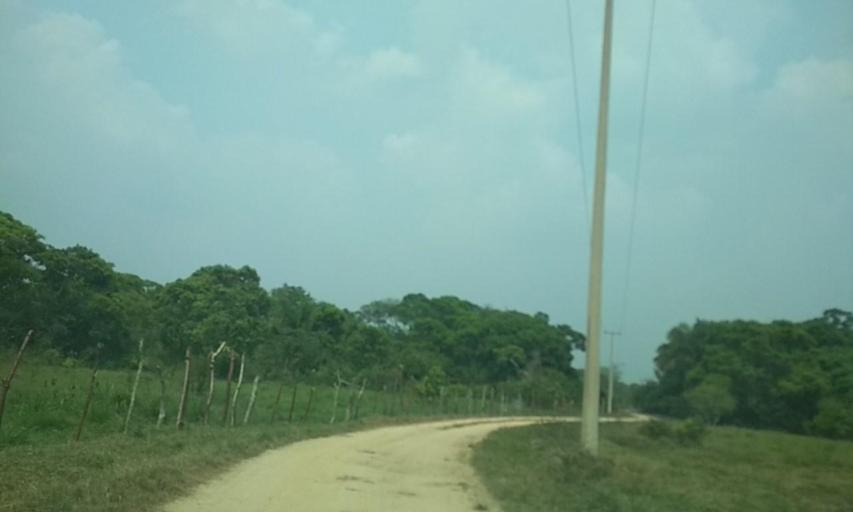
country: MX
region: Veracruz
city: Las Choapas
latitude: 17.8148
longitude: -94.0608
